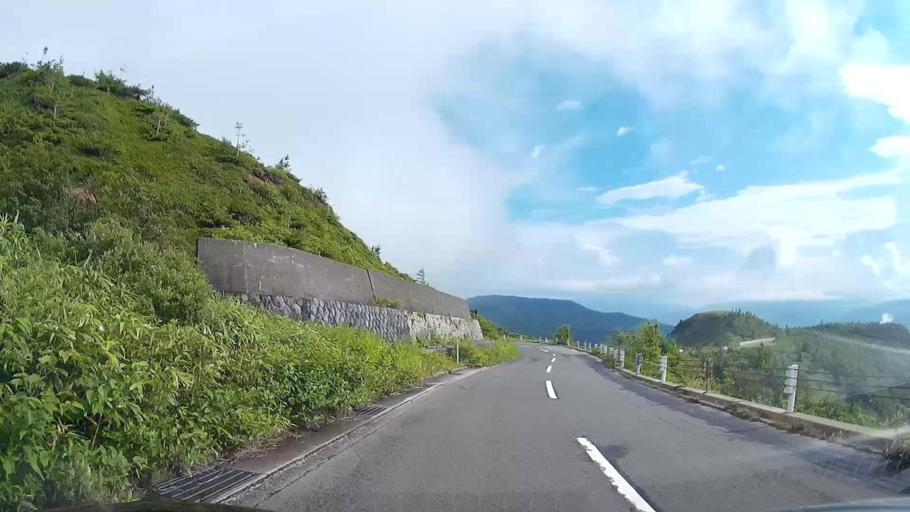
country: JP
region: Nagano
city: Nakano
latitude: 36.6448
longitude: 138.5249
